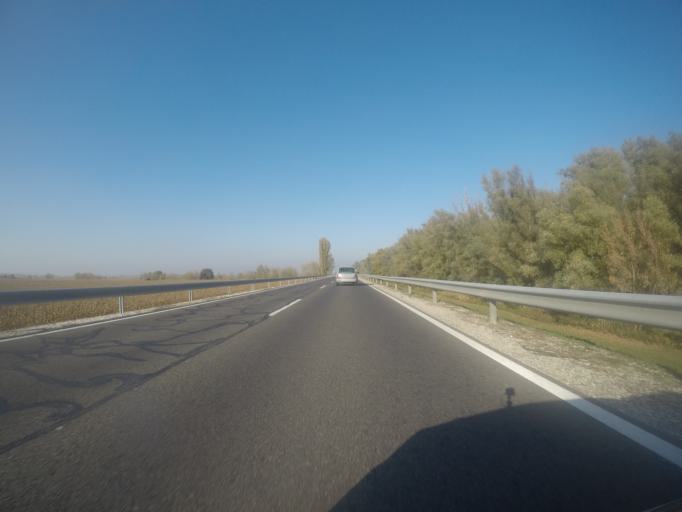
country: HU
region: Fejer
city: Ivancsa
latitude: 47.1878
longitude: 18.8705
